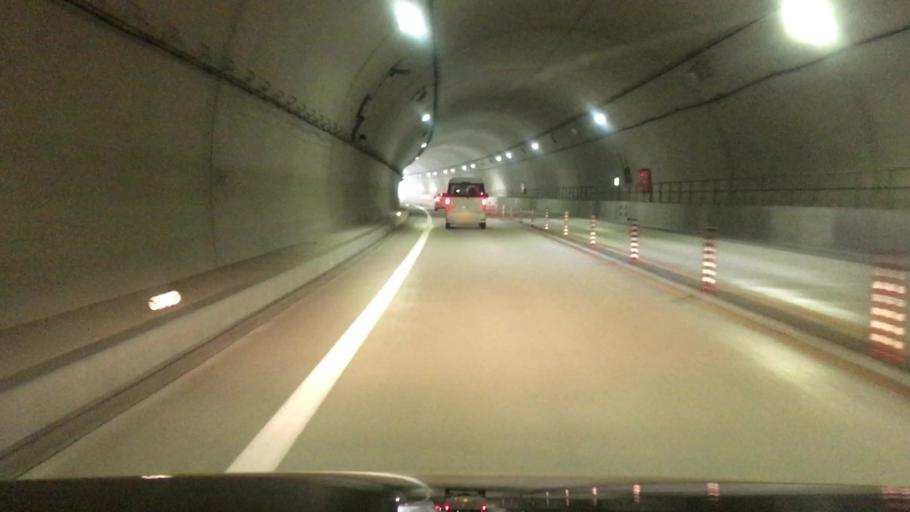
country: JP
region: Hyogo
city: Toyooka
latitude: 35.4249
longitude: 134.7642
